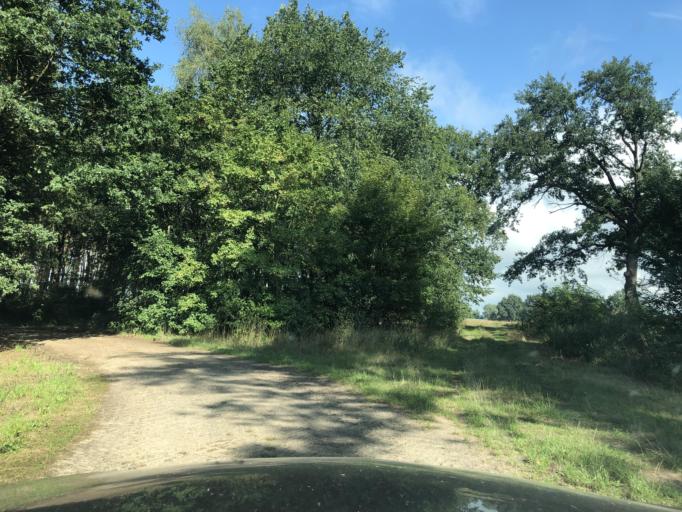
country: DE
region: Brandenburg
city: Schlepzig
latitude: 52.0158
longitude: 13.9599
